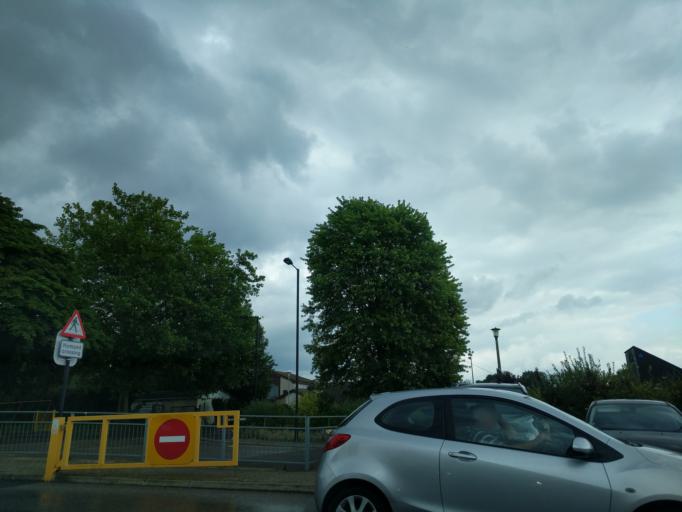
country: GB
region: England
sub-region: Suffolk
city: Lakenheath
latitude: 52.3427
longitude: 0.5136
